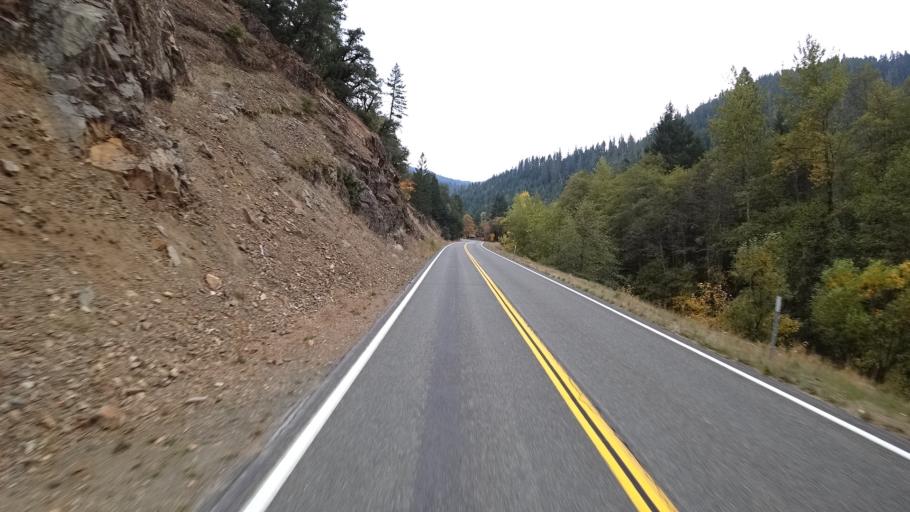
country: US
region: California
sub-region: Siskiyou County
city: Happy Camp
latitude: 41.8897
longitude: -123.4329
